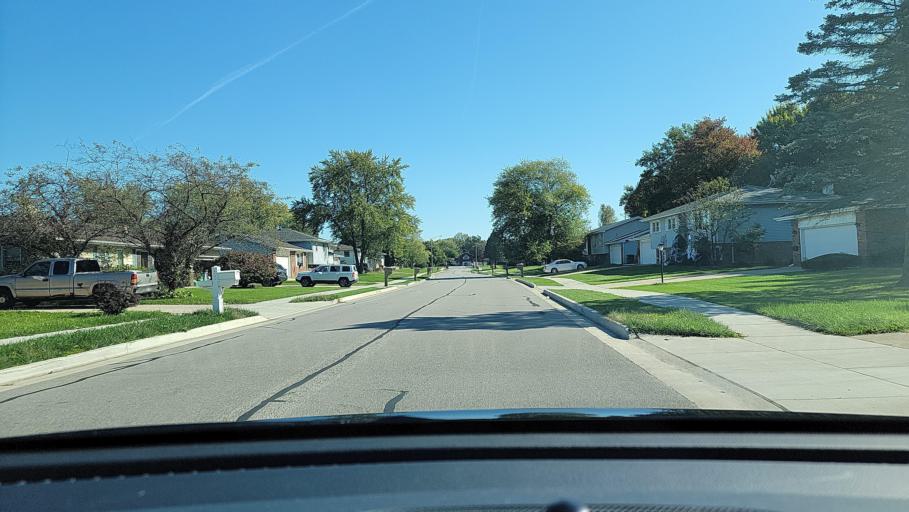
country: US
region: Indiana
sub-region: Porter County
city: Portage
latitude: 41.5725
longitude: -87.1675
